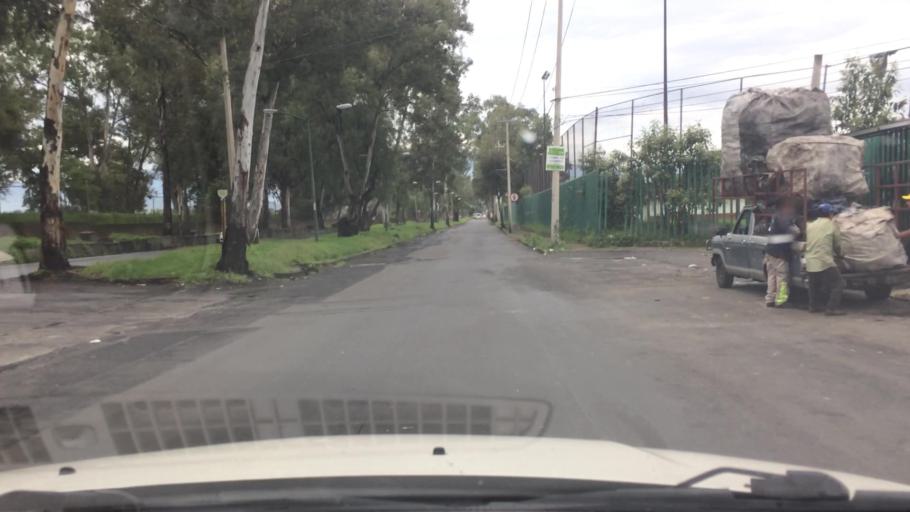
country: MX
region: Mexico City
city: Iztapalapa
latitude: 19.3140
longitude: -99.0999
